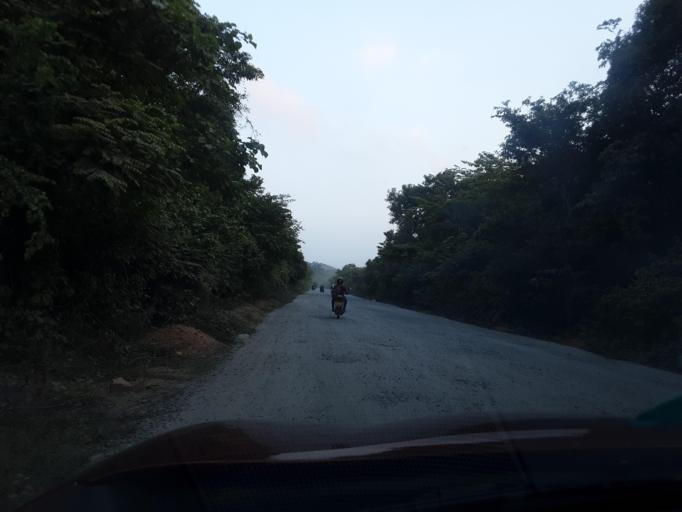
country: LK
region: Central
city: Dambulla
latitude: 7.8087
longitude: 80.7809
